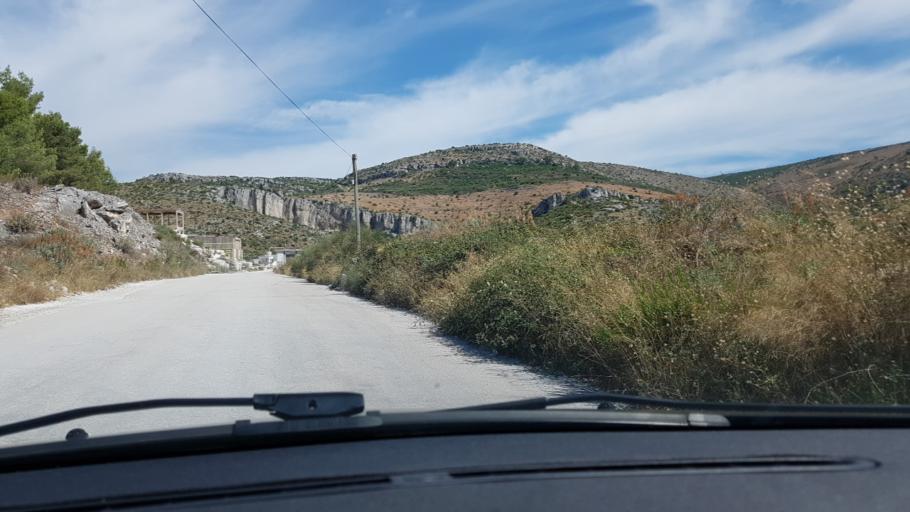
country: HR
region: Splitsko-Dalmatinska
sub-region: Grad Trogir
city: Trogir
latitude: 43.5286
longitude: 16.2288
